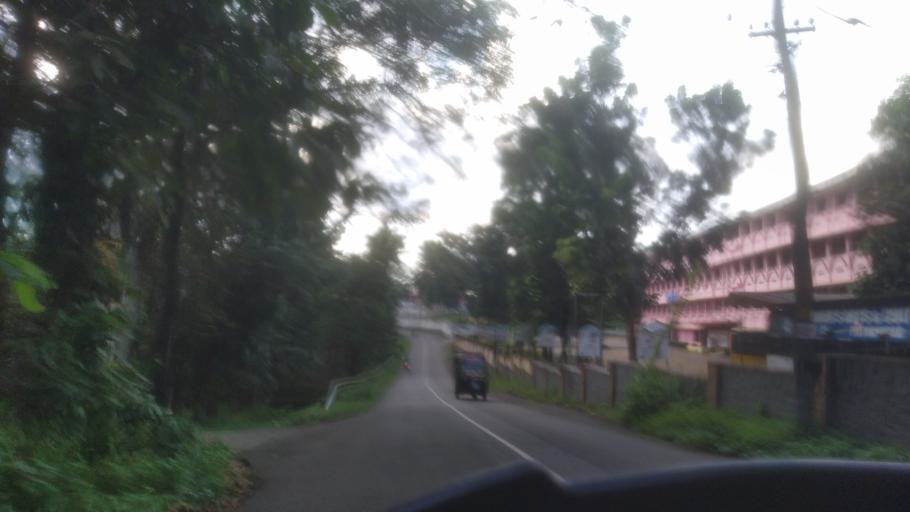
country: IN
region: Kerala
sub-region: Ernakulam
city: Kotamangalam
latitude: 10.0069
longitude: 76.6732
